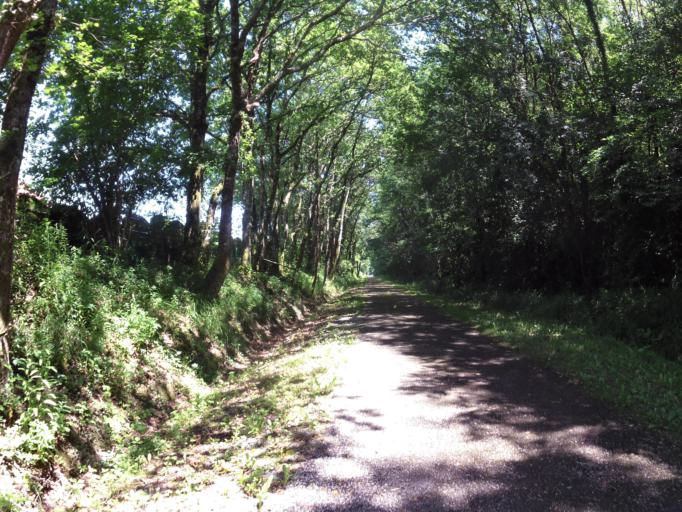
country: FR
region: Aquitaine
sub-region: Departement des Pyrenees-Atlantiques
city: Salies-de-Bearn
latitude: 43.4652
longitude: -0.9540
